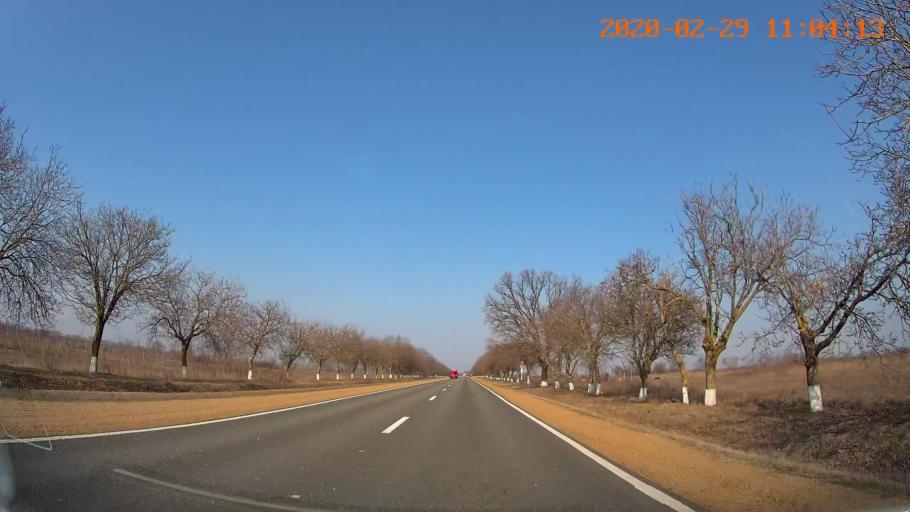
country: MD
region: Criuleni
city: Criuleni
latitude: 47.1862
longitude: 29.2049
